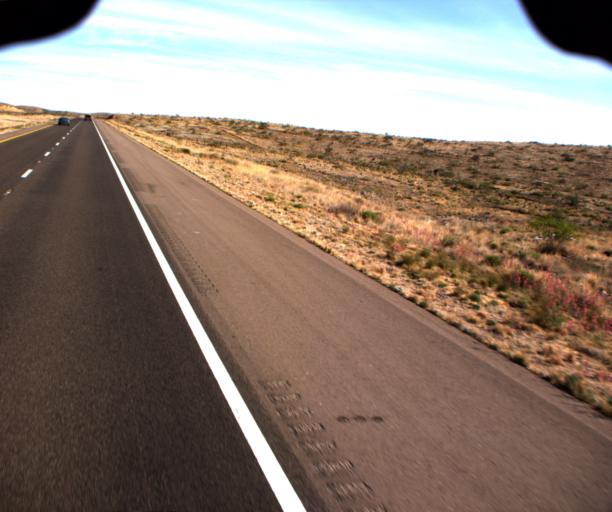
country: US
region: Arizona
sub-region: Cochise County
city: Willcox
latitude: 32.4237
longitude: -109.6626
